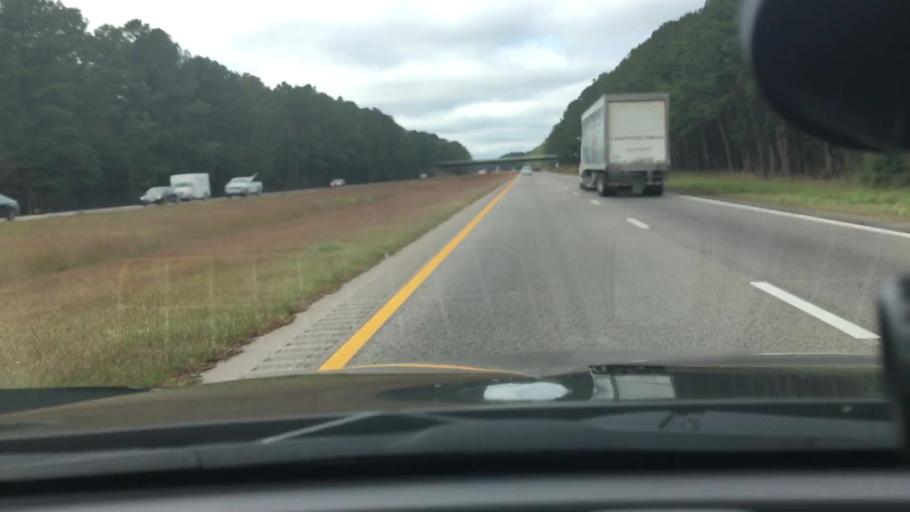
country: US
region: North Carolina
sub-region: Wilson County
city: Lucama
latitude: 35.7807
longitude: -78.0824
